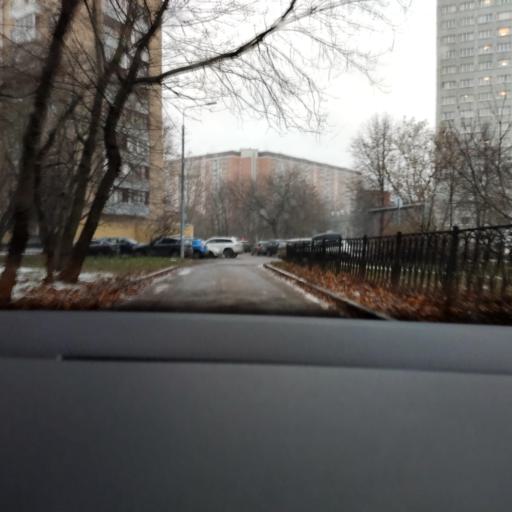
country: RU
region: Moscow
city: Leonovo
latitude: 55.8497
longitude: 37.6465
